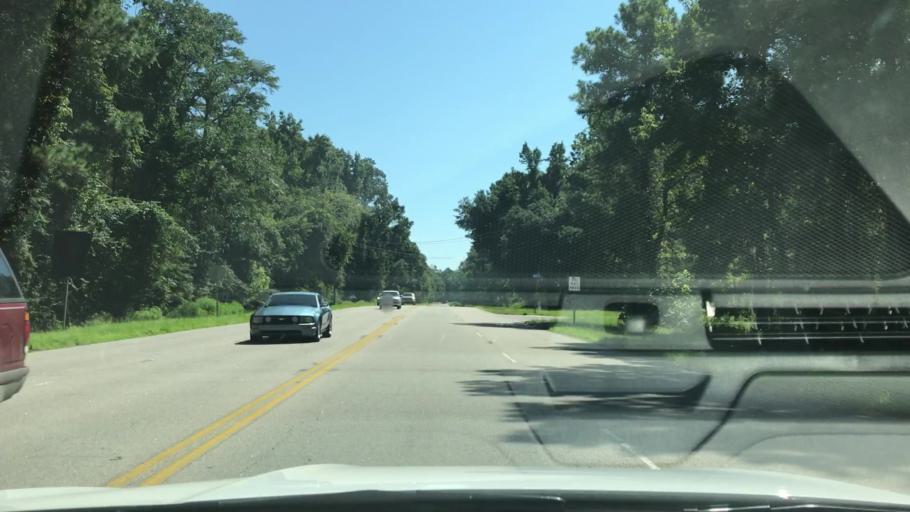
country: US
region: South Carolina
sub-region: Horry County
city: Conway
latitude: 33.8380
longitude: -79.0408
